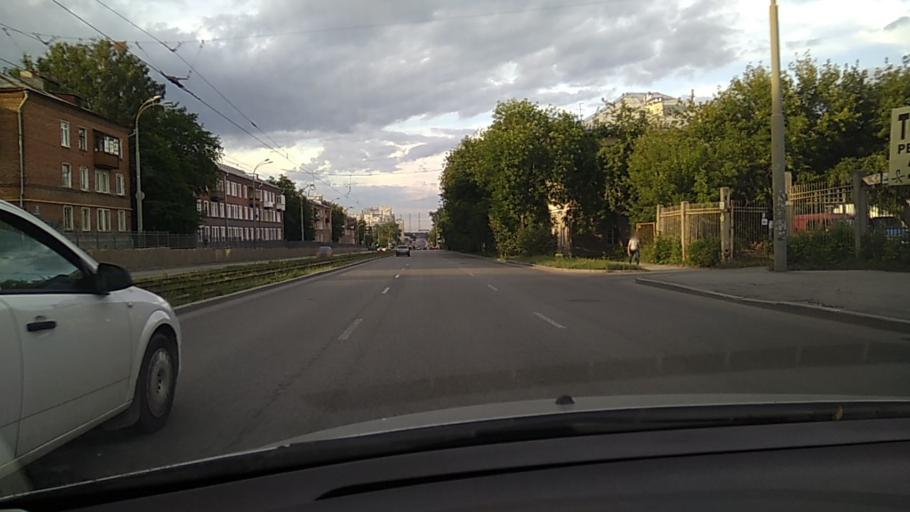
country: RU
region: Sverdlovsk
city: Yekaterinburg
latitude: 56.8954
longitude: 60.5753
